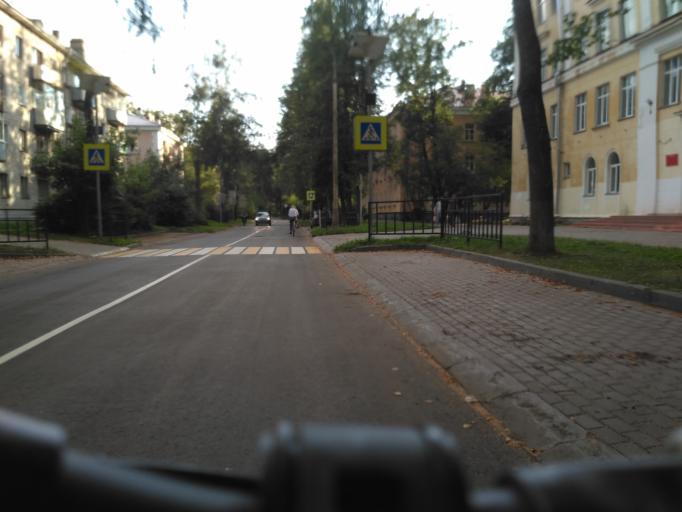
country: RU
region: Moskovskaya
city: Dubna
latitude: 56.7492
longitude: 37.1948
